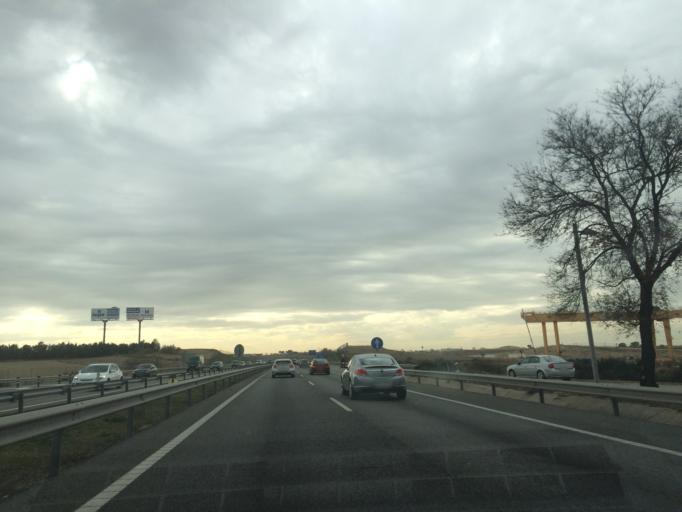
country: ES
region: Madrid
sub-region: Provincia de Madrid
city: Mostoles
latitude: 40.3163
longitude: -3.8978
